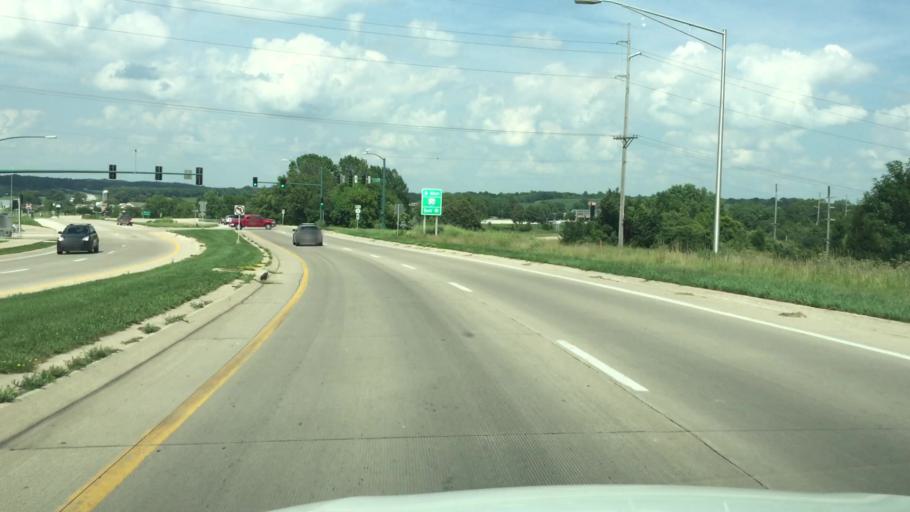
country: US
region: Iowa
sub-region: Johnson County
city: Iowa City
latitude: 41.6847
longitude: -91.5012
